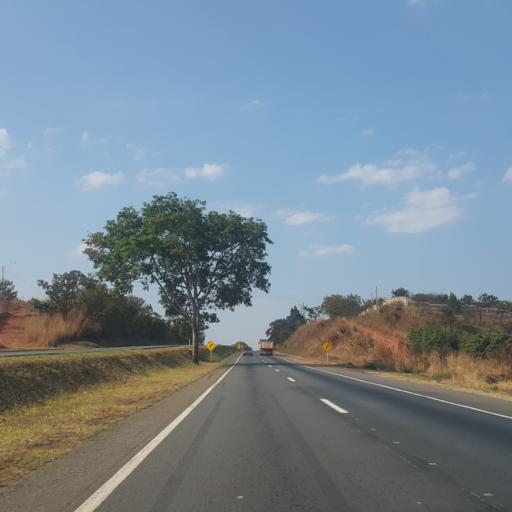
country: BR
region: Goias
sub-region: Abadiania
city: Abadiania
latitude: -16.0951
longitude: -48.5184
